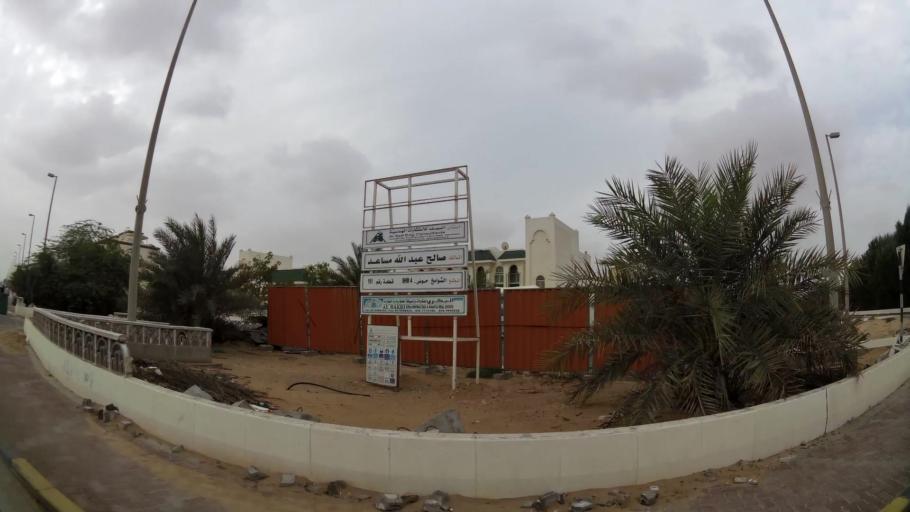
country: AE
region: Abu Dhabi
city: Abu Dhabi
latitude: 24.3539
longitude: 54.6533
